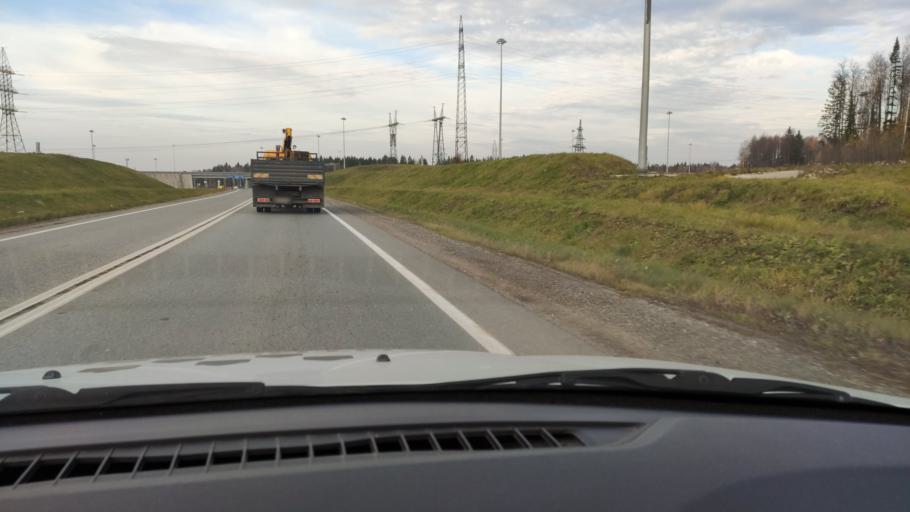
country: RU
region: Perm
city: Novyye Lyady
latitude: 58.0444
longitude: 56.4375
